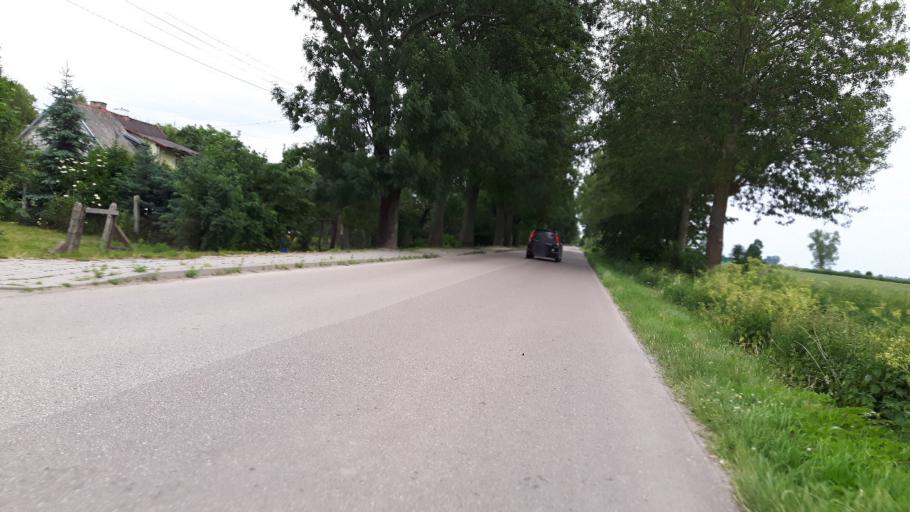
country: PL
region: Warmian-Masurian Voivodeship
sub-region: Powiat elblaski
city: Gronowo Elblaskie
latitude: 54.2157
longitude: 19.2613
